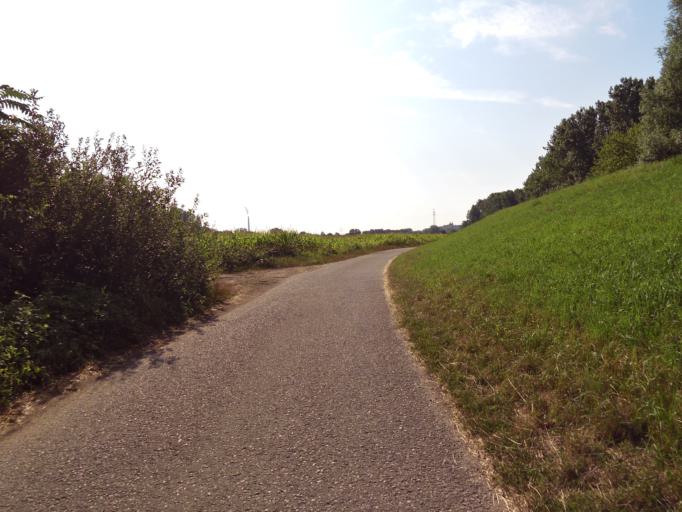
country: DE
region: Rheinland-Pfalz
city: Ludwigshafen am Rhein
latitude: 49.5405
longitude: 8.4336
